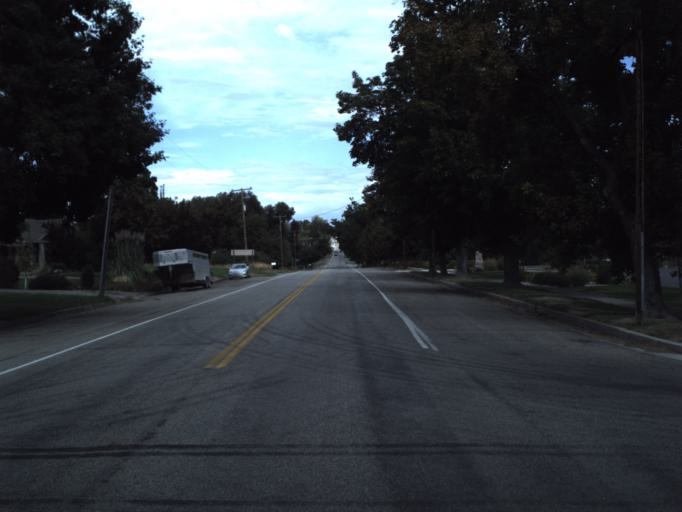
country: US
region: Utah
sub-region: Cache County
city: Mendon
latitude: 41.7079
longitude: -111.9793
